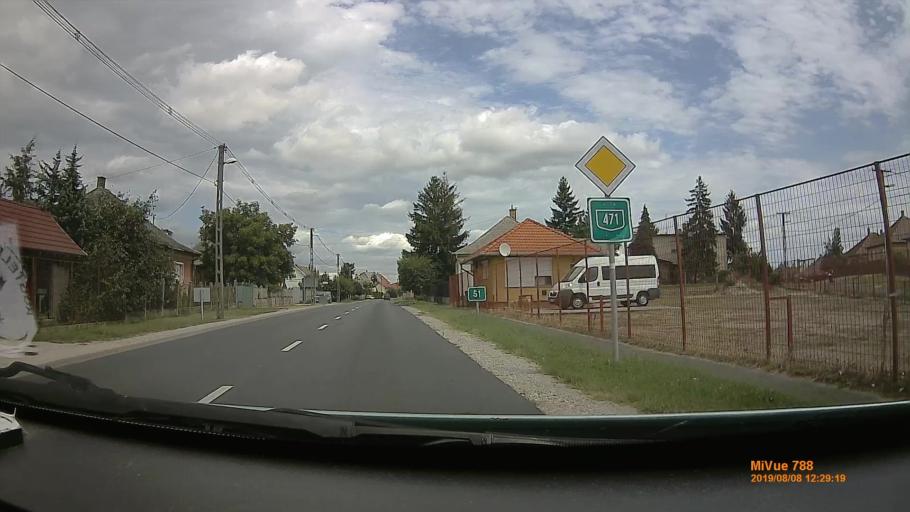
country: HU
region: Szabolcs-Szatmar-Bereg
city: Nyirbator
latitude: 47.8344
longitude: 22.1183
